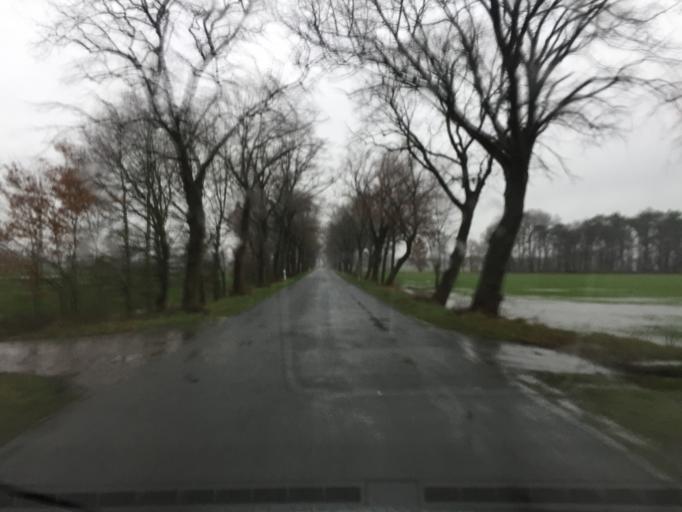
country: DE
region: Lower Saxony
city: Barenburg
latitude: 52.6455
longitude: 8.8262
